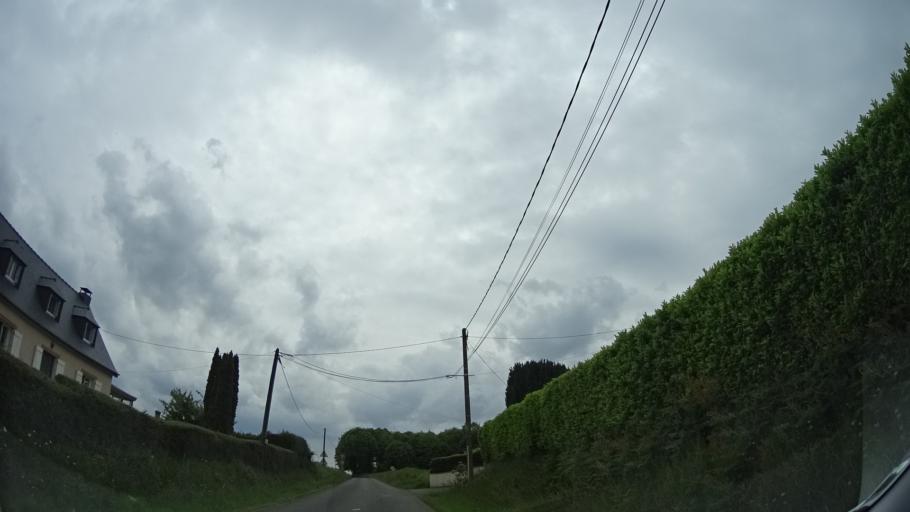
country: FR
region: Brittany
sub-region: Departement d'Ille-et-Vilaine
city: Tinteniac
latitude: 48.2790
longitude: -1.8515
